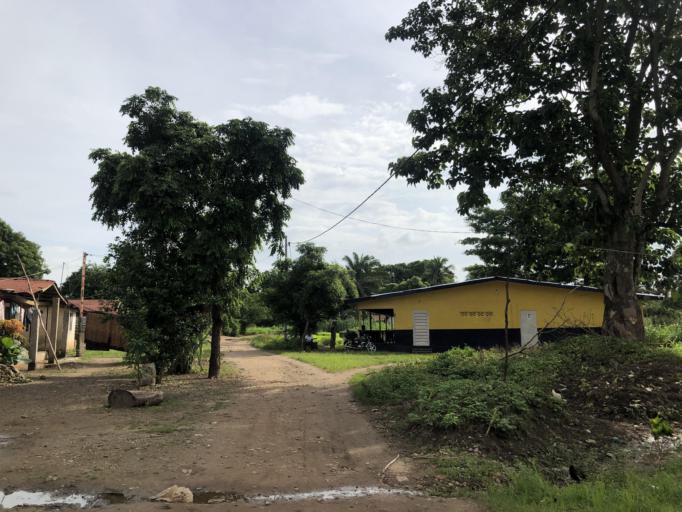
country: SL
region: Northern Province
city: Bumbuna
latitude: 9.0460
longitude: -11.7494
